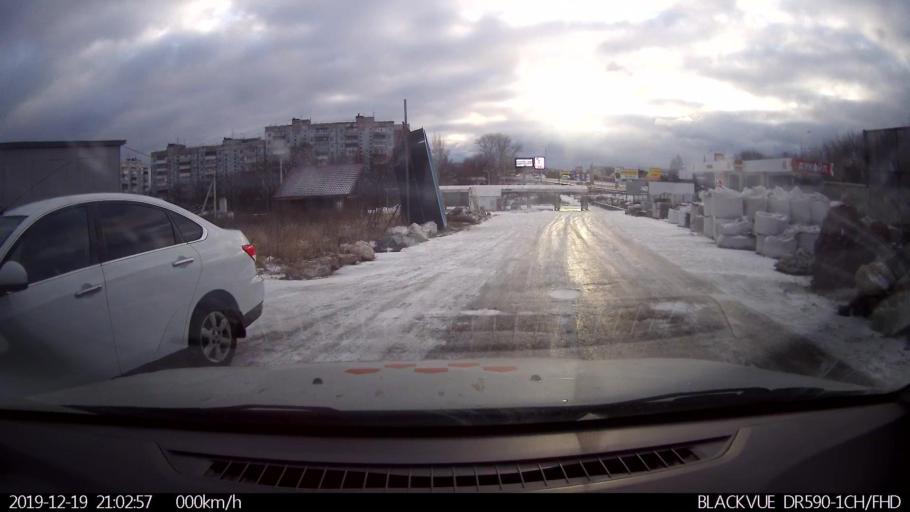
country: RU
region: Nizjnij Novgorod
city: Afonino
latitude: 56.2753
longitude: 44.0844
